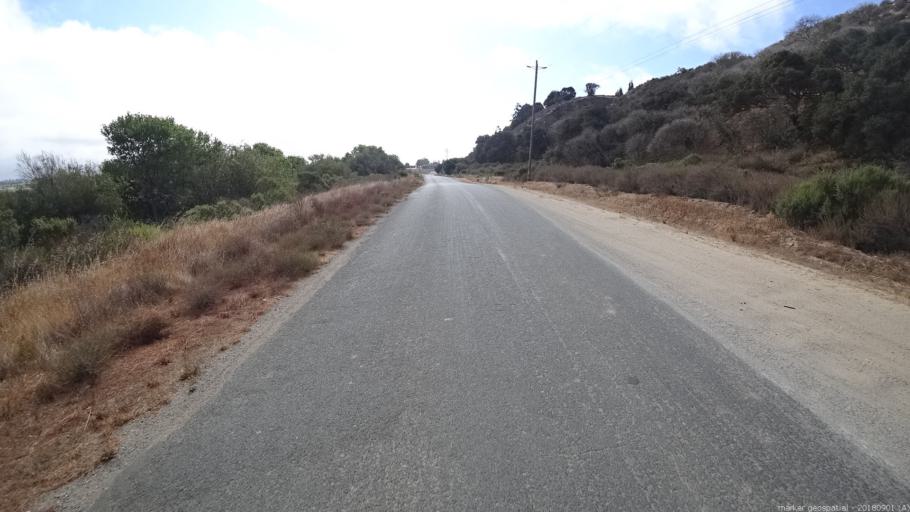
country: US
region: California
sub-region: Monterey County
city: Soledad
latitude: 36.3995
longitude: -121.3760
